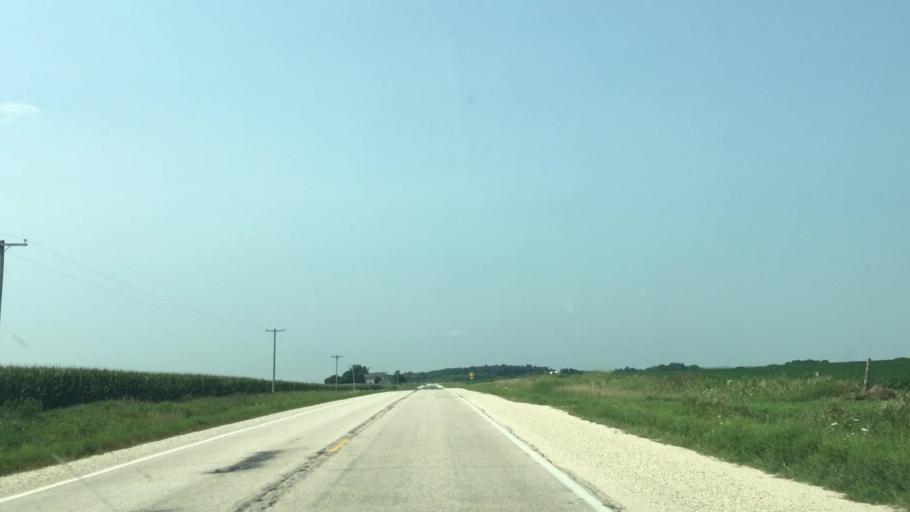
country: US
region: Iowa
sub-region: Fayette County
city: West Union
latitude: 43.0248
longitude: -91.8274
